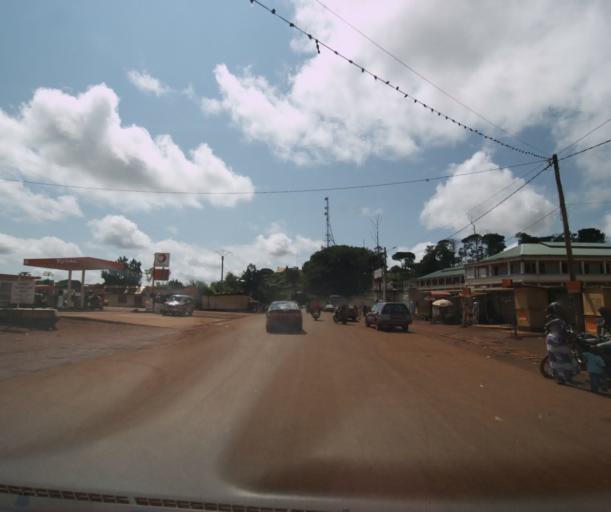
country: CM
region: West
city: Foumban
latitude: 5.7313
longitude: 10.8777
